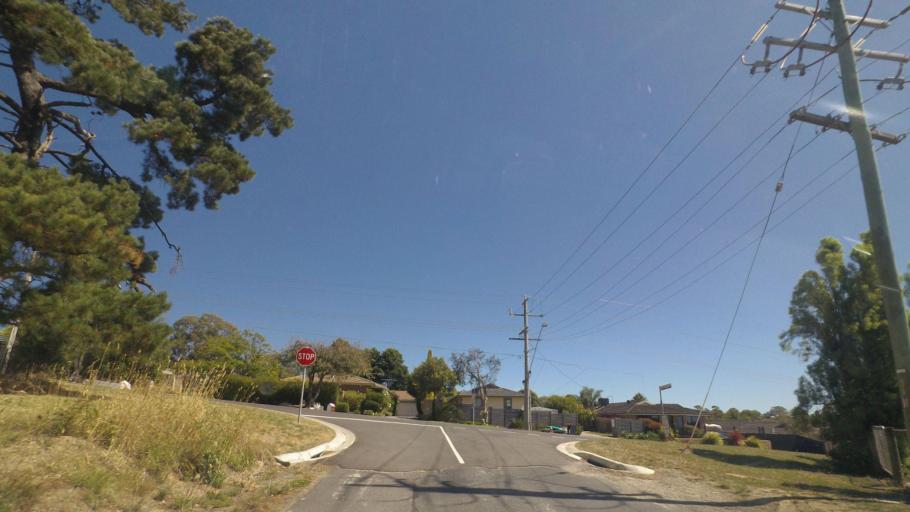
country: AU
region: Victoria
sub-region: Yarra Ranges
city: Chirnside Park
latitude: -37.7441
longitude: 145.3241
